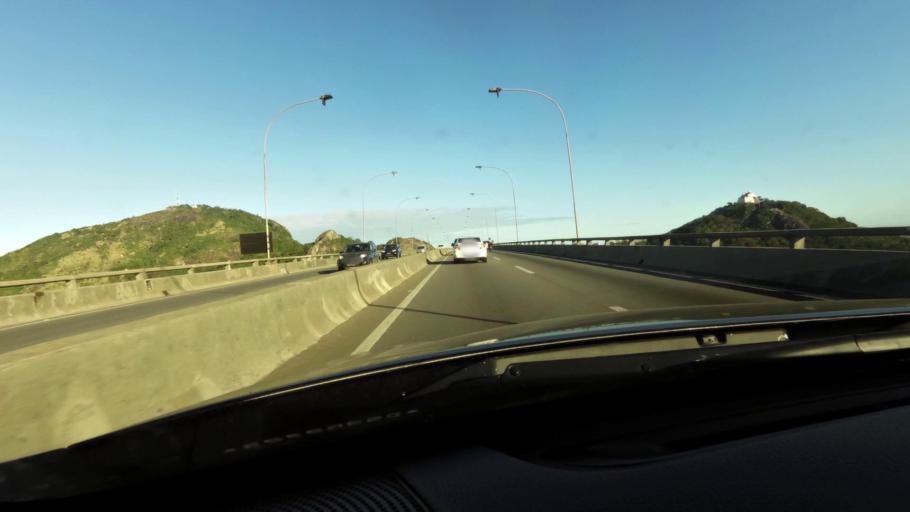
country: BR
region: Espirito Santo
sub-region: Vila Velha
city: Vila Velha
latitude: -20.3203
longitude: -40.2847
